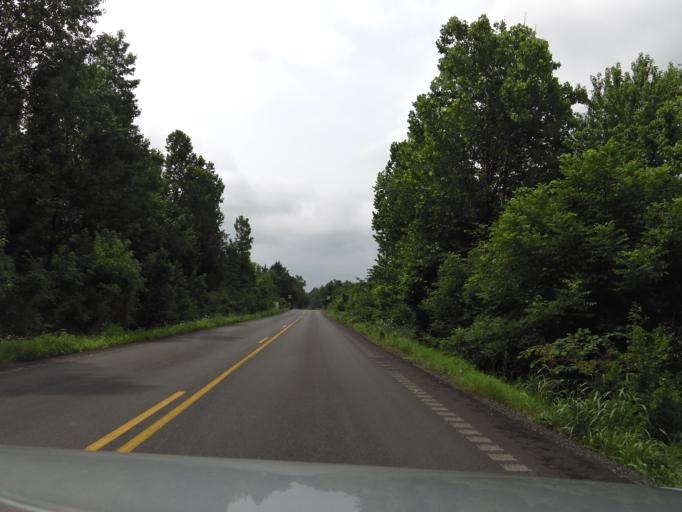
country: US
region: Kentucky
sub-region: Hopkins County
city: Madisonville
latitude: 37.3099
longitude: -87.3680
